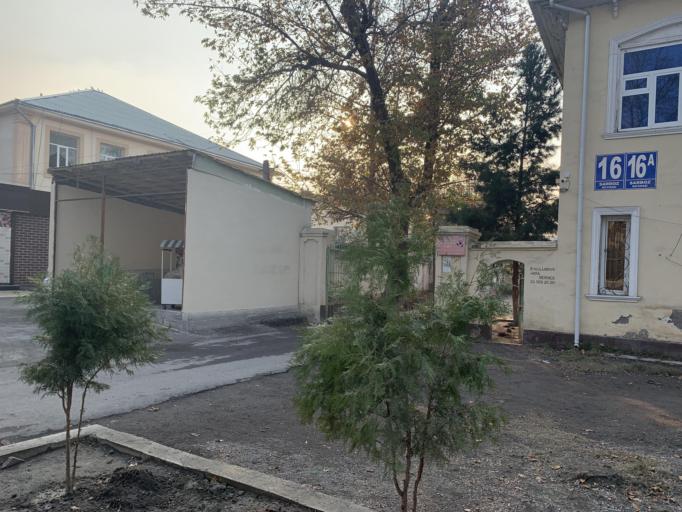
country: UZ
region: Fergana
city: Qo`qon
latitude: 40.5326
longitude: 70.9378
